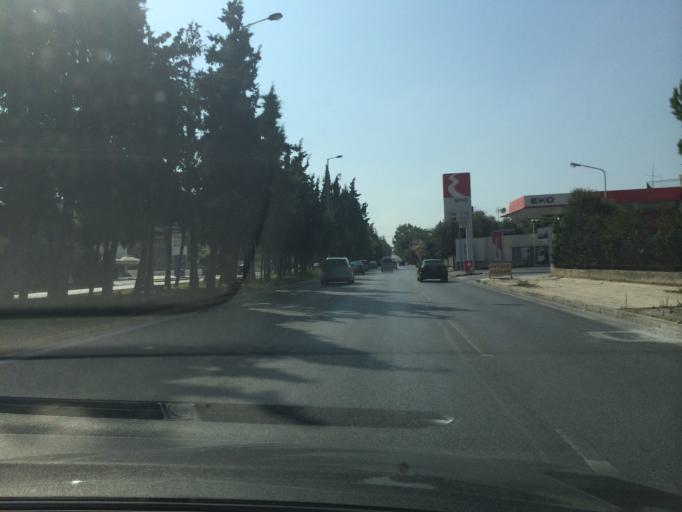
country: GR
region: Attica
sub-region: Nomarchia Anatolikis Attikis
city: Voula
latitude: 37.8328
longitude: 23.7725
